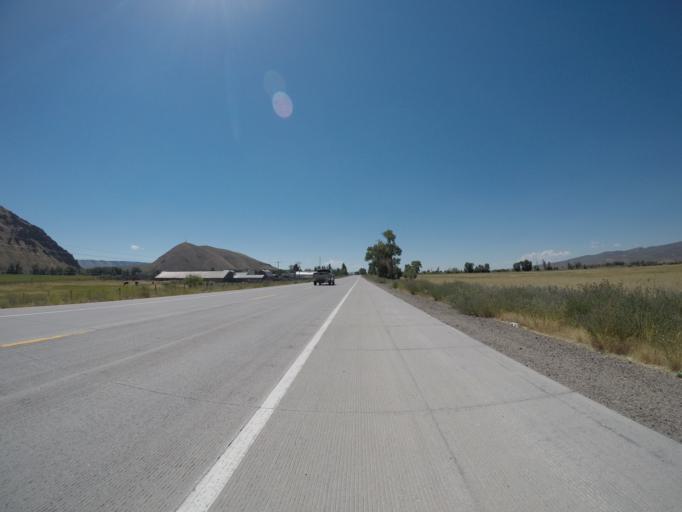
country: US
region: Idaho
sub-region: Bear Lake County
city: Montpelier
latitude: 42.1009
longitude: -110.9532
